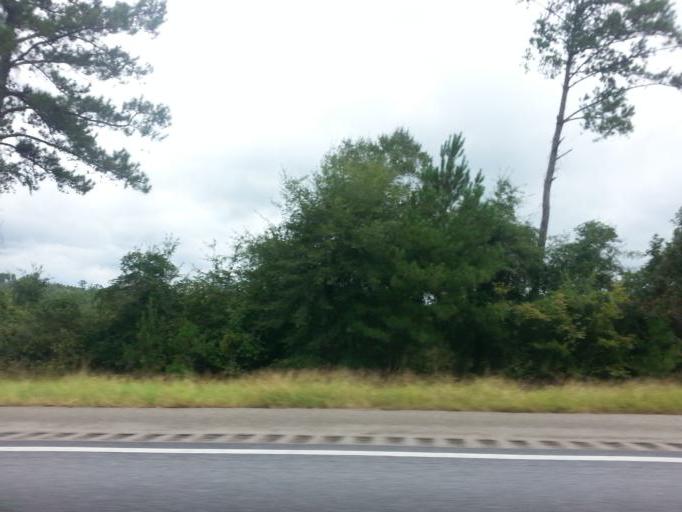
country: US
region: Alabama
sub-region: Conecuh County
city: Evergreen
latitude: 31.3166
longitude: -87.1477
